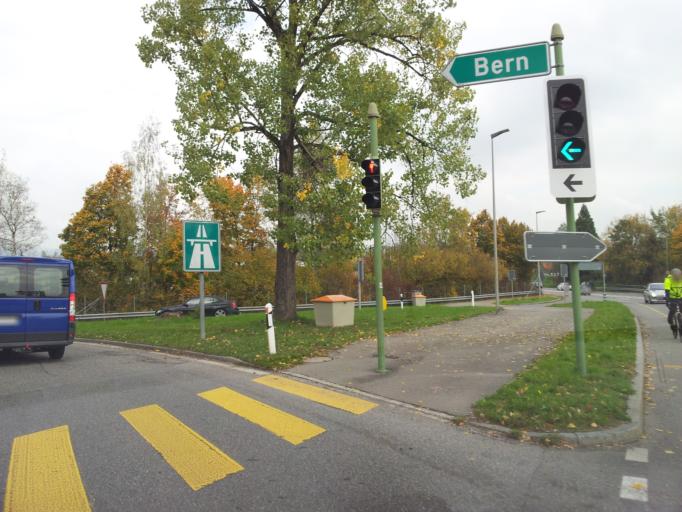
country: CH
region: Bern
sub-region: Bern-Mittelland District
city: Rubigen
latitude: 46.8902
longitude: 7.5404
